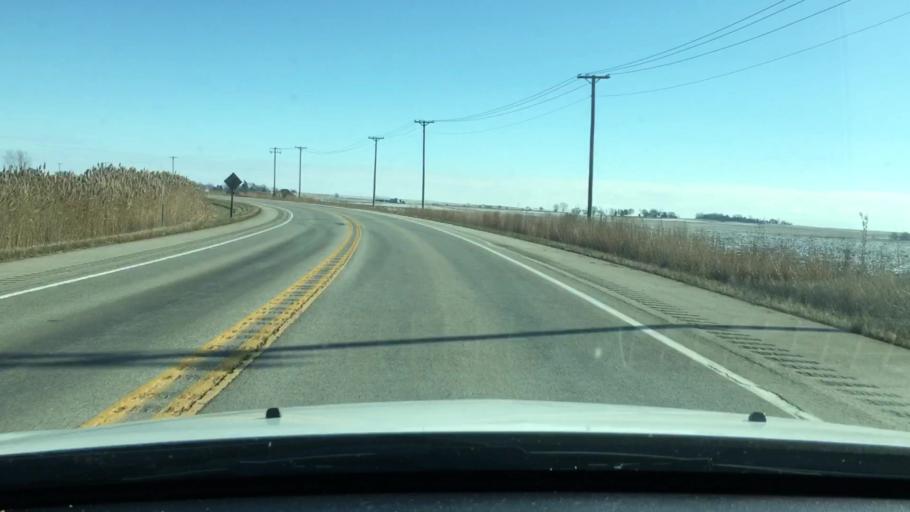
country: US
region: Illinois
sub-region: DeKalb County
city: Malta
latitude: 42.0014
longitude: -88.9341
